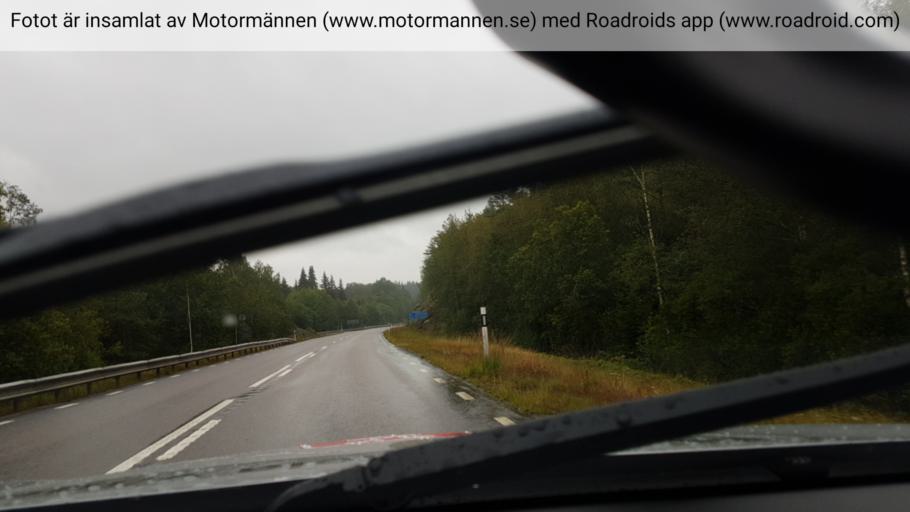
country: SE
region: Vaestra Goetaland
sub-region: Dals-Ed Kommun
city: Ed
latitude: 58.8754
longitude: 11.8578
